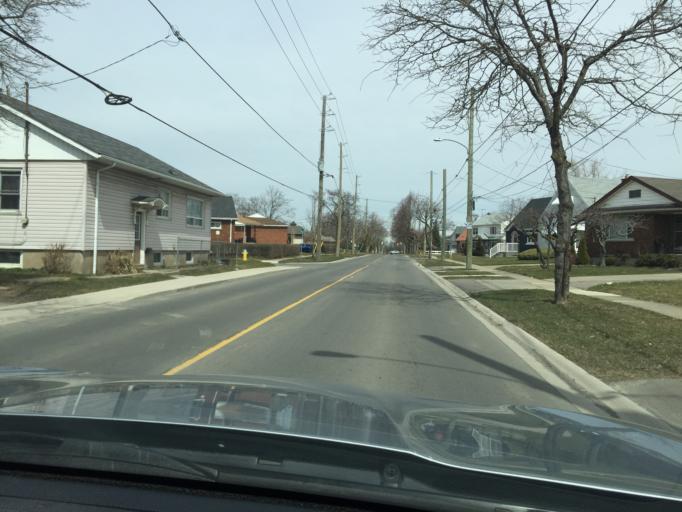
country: CA
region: Ontario
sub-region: Regional Municipality of Niagara
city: St. Catharines
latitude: 43.1794
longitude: -79.2205
